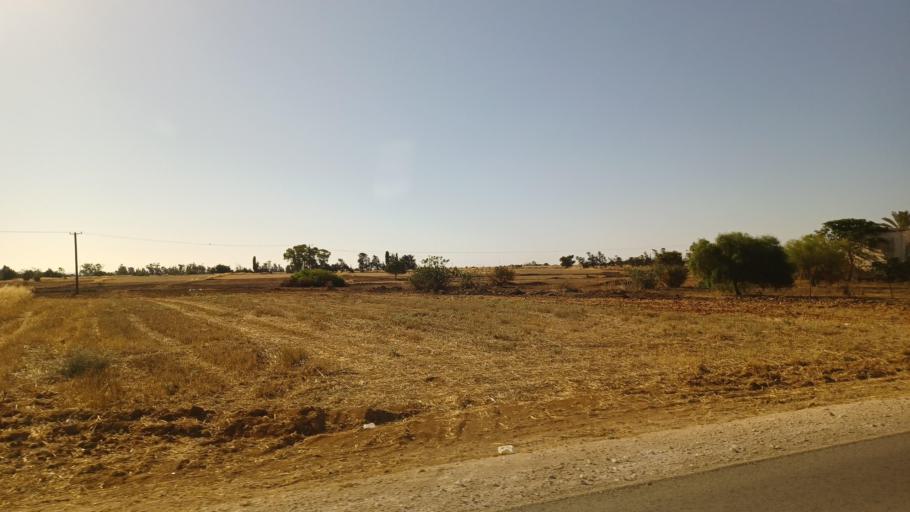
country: CY
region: Larnaka
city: Pergamos
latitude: 35.0317
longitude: 33.7054
